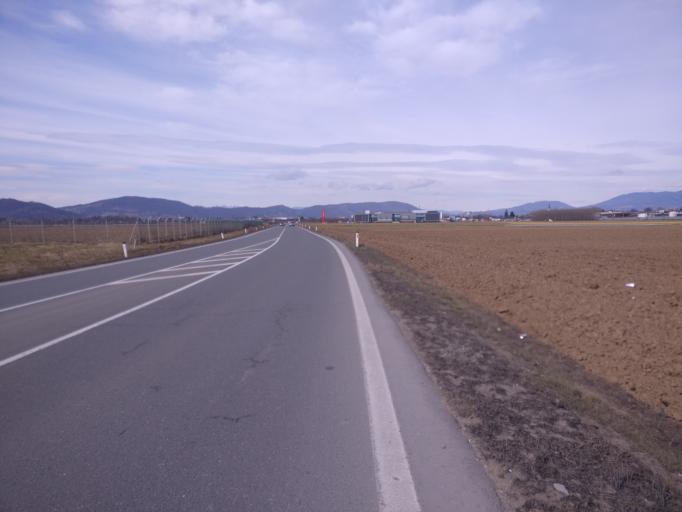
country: AT
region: Styria
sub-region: Politischer Bezirk Graz-Umgebung
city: Feldkirchen bei Graz
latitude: 47.0005
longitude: 15.4453
